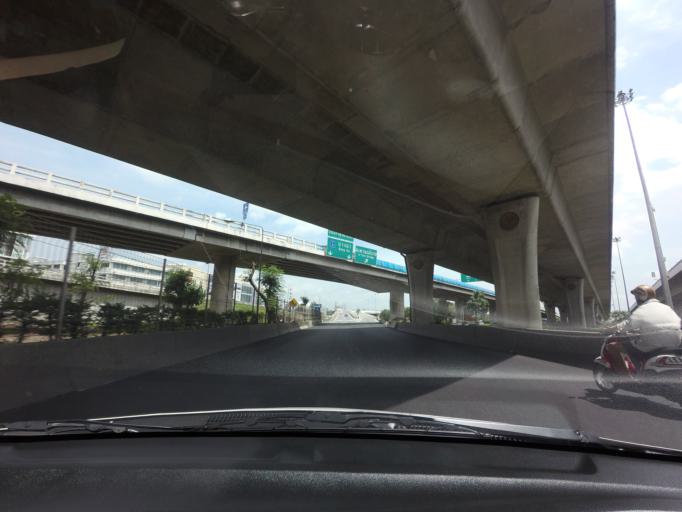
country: TH
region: Bangkok
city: Khan Na Yao
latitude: 13.8274
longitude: 100.6745
